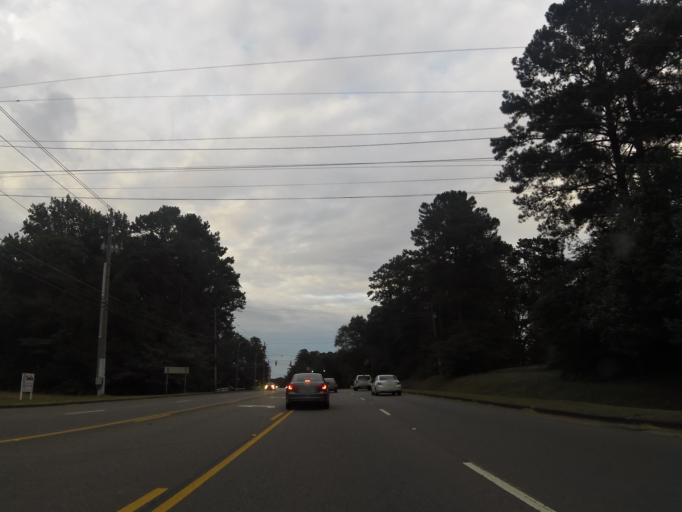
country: US
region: Alabama
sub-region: Jefferson County
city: Trussville
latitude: 33.6102
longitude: -86.6263
